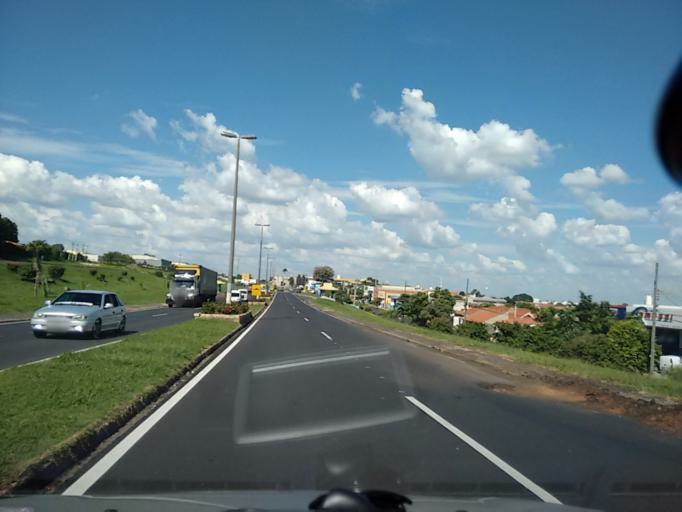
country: BR
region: Sao Paulo
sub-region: Pompeia
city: Pompeia
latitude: -22.1038
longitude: -50.1910
